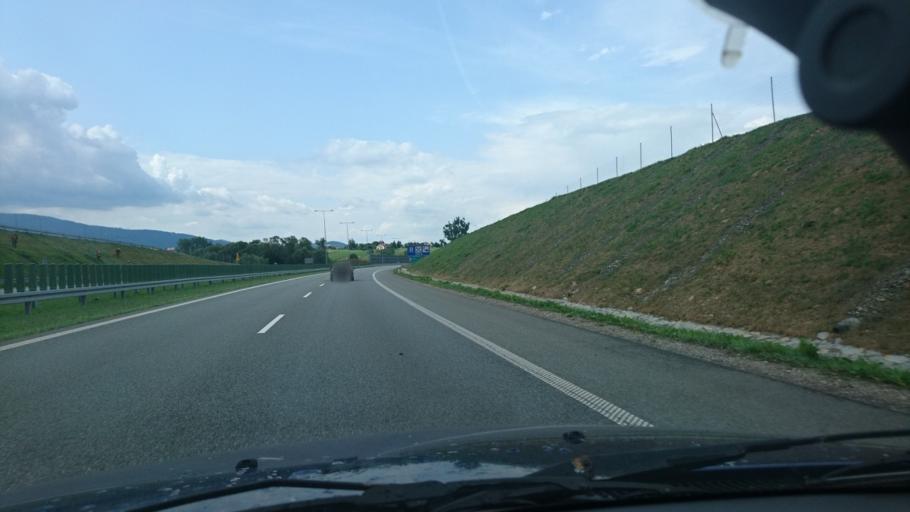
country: PL
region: Silesian Voivodeship
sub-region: Powiat zywiecki
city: Lodygowice
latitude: 49.7041
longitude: 19.1234
